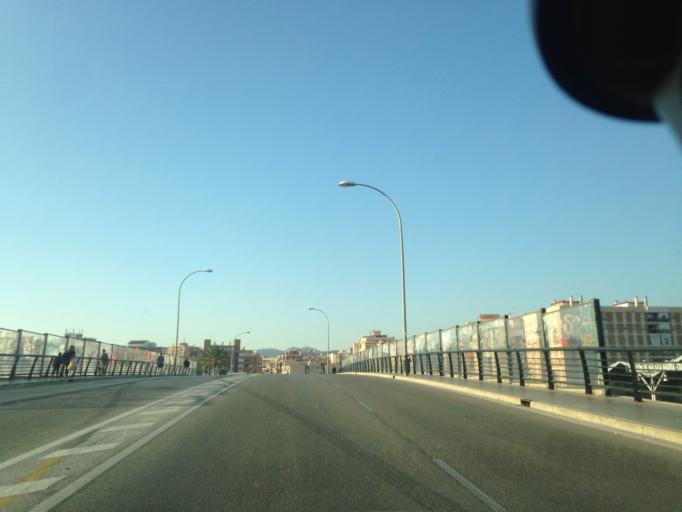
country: ES
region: Andalusia
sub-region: Provincia de Malaga
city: Malaga
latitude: 36.7090
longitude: -4.4365
